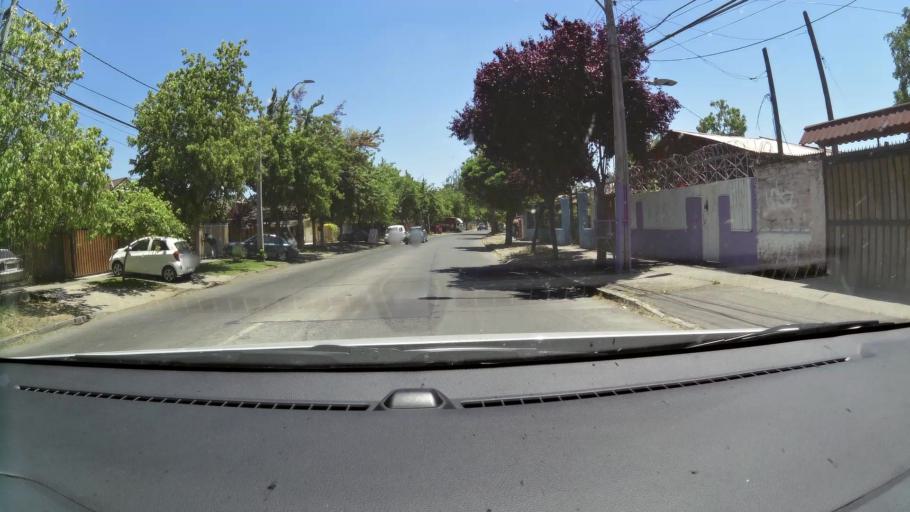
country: CL
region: Santiago Metropolitan
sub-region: Provincia de Maipo
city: San Bernardo
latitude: -33.6012
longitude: -70.6964
